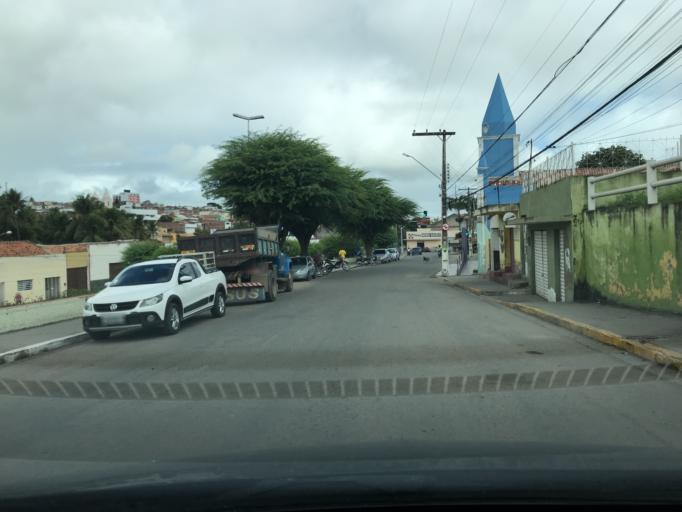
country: BR
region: Pernambuco
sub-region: Bezerros
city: Bezerros
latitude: -8.2321
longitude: -35.7525
